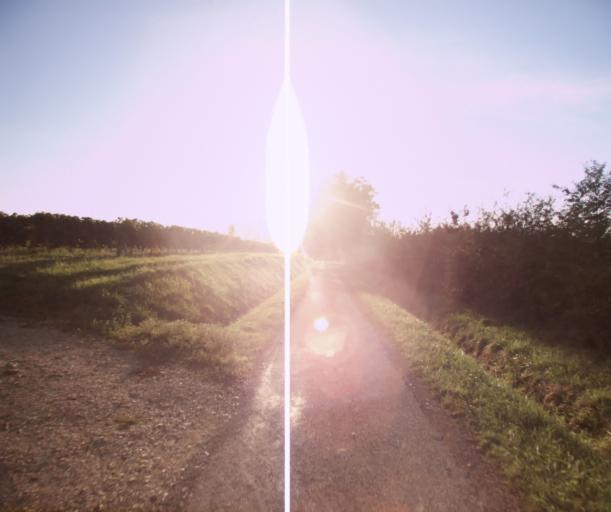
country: FR
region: Midi-Pyrenees
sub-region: Departement du Gers
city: Eauze
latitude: 43.8750
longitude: 0.0237
